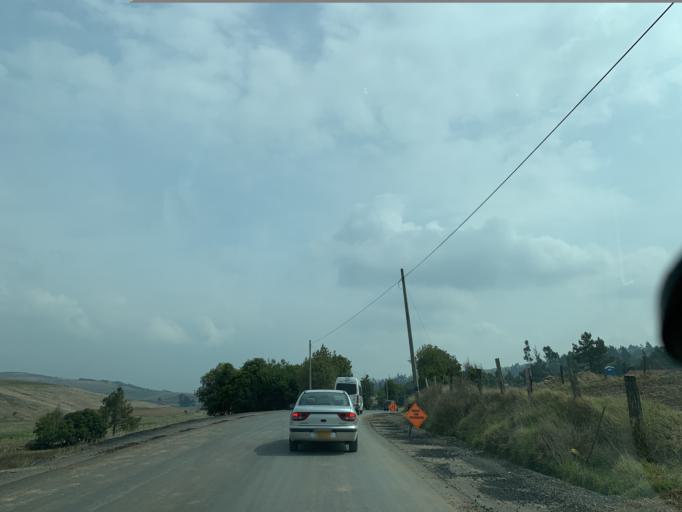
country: CO
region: Boyaca
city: Tunja
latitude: 5.5332
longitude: -73.3079
